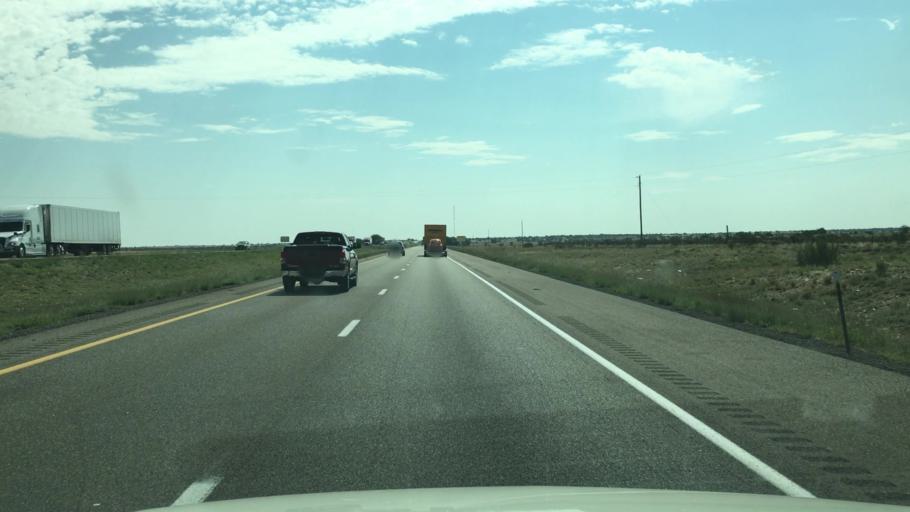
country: US
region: New Mexico
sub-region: Guadalupe County
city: Santa Rosa
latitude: 34.9739
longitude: -104.9457
